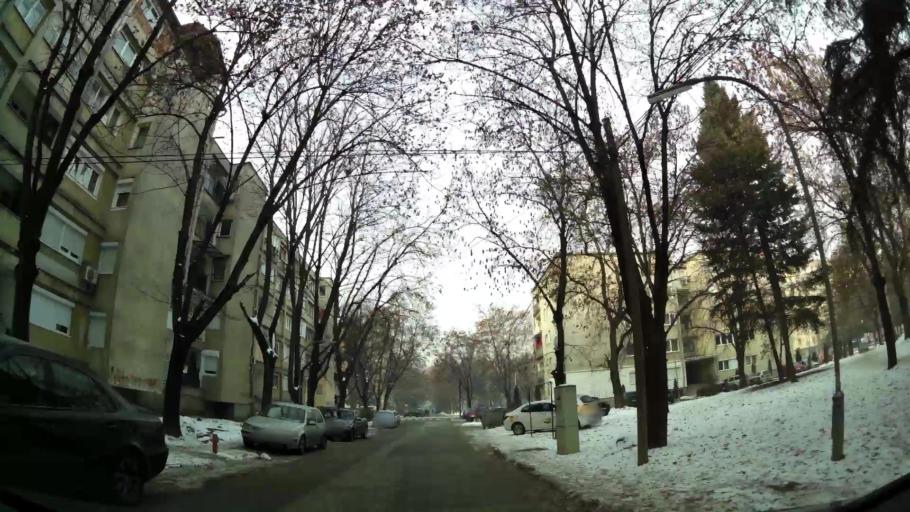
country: MK
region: Cair
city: Cair
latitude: 42.0195
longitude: 21.4443
